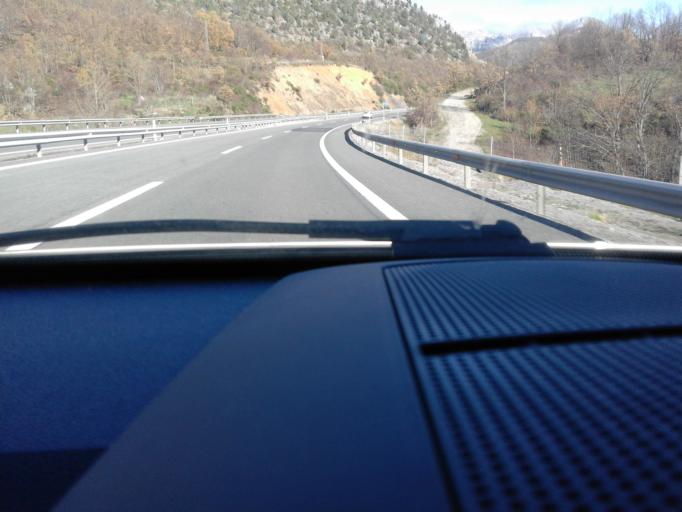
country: ES
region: Castille and Leon
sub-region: Provincia de Leon
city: Sena de Luna
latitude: 42.8720
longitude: -5.8859
